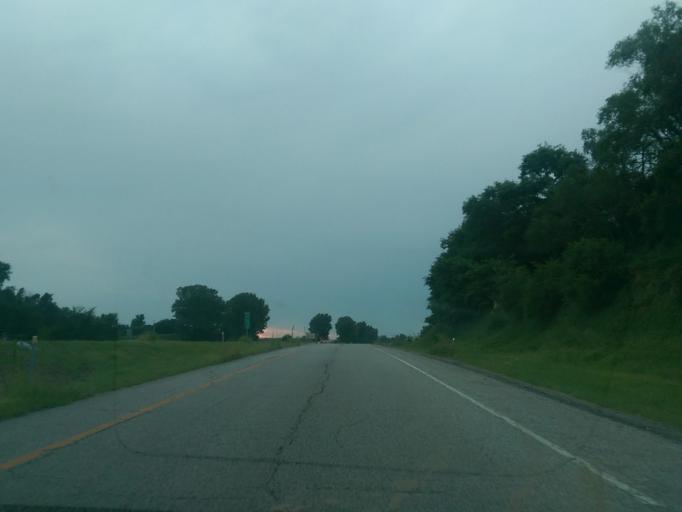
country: US
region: Missouri
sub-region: Holt County
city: Oregon
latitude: 40.0462
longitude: -95.1398
